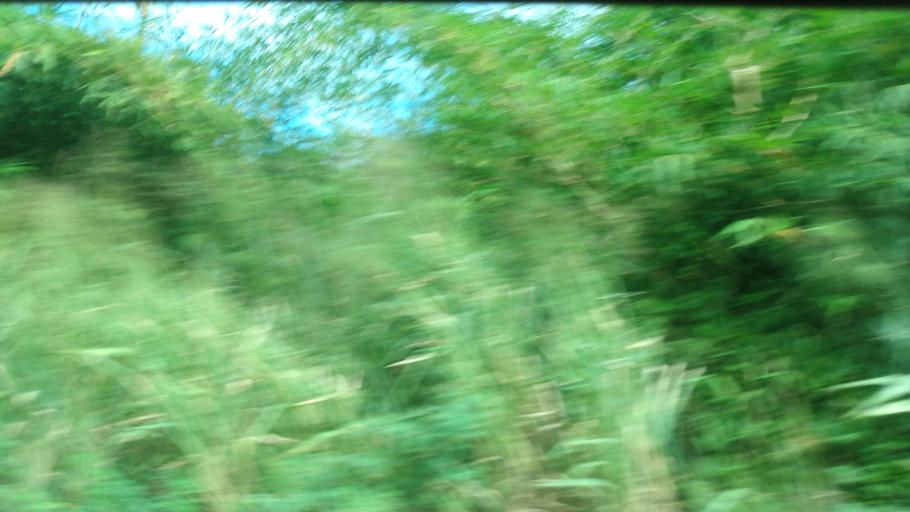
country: BR
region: Pernambuco
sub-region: Catende
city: Catende
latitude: -8.6960
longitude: -35.6588
